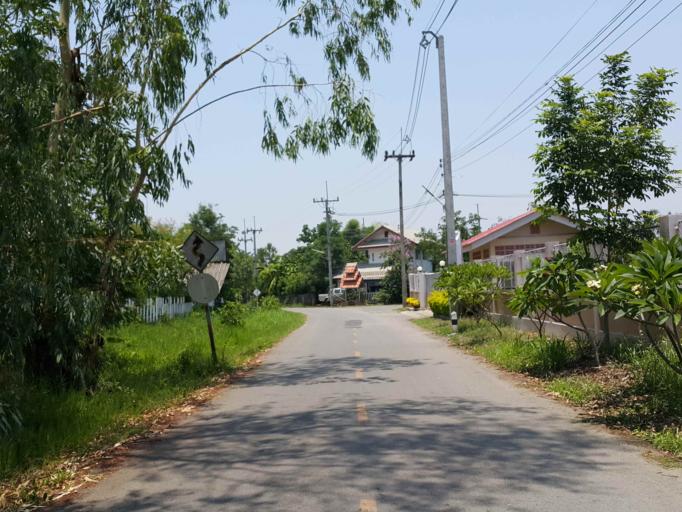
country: TH
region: Chiang Mai
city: San Kamphaeng
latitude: 18.7983
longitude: 99.1127
